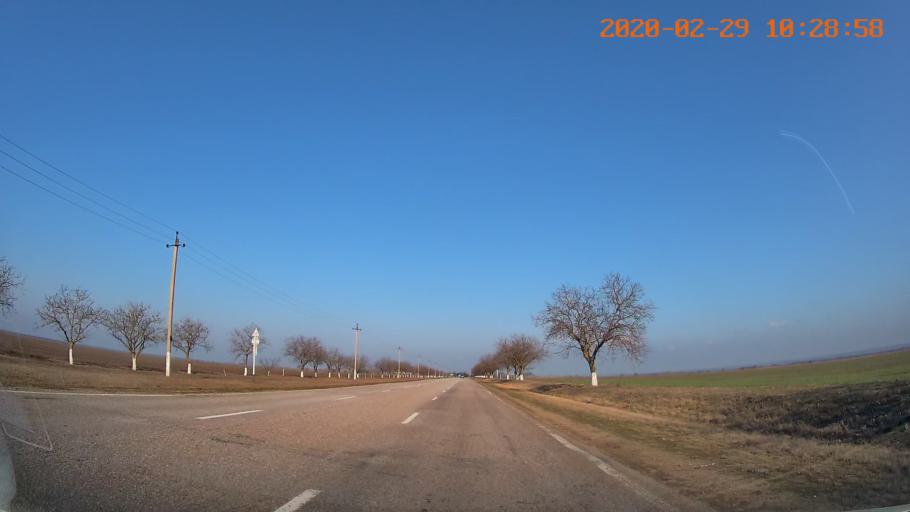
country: MD
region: Telenesti
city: Tiraspolul Nou
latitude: 46.9178
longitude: 29.5883
